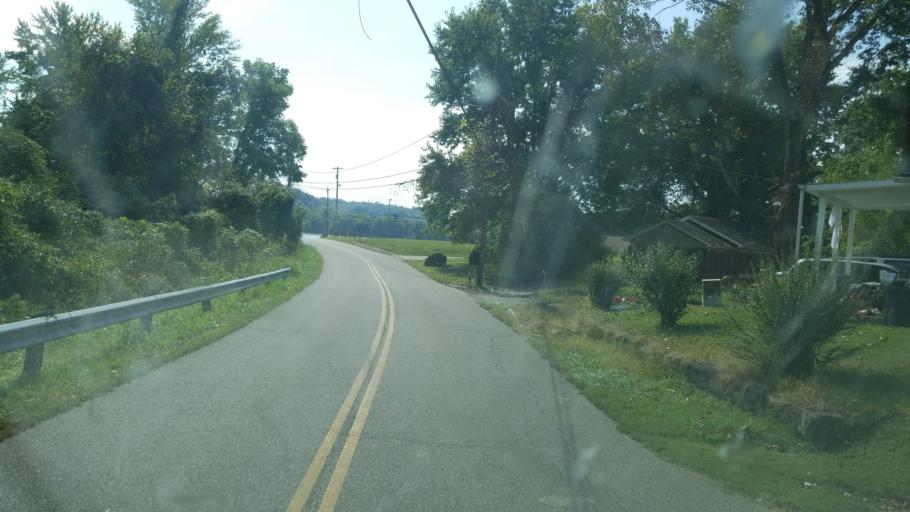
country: US
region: Ohio
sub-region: Gallia County
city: Gallipolis
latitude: 38.8183
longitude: -82.1886
